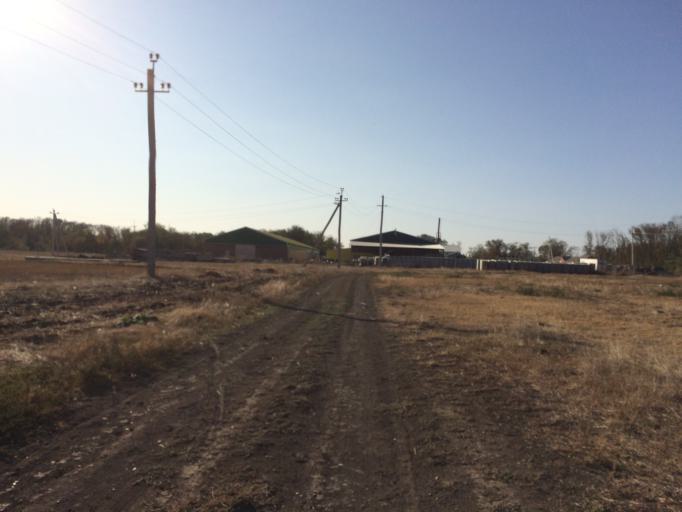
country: RU
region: Rostov
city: Gigant
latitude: 46.5127
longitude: 41.1872
